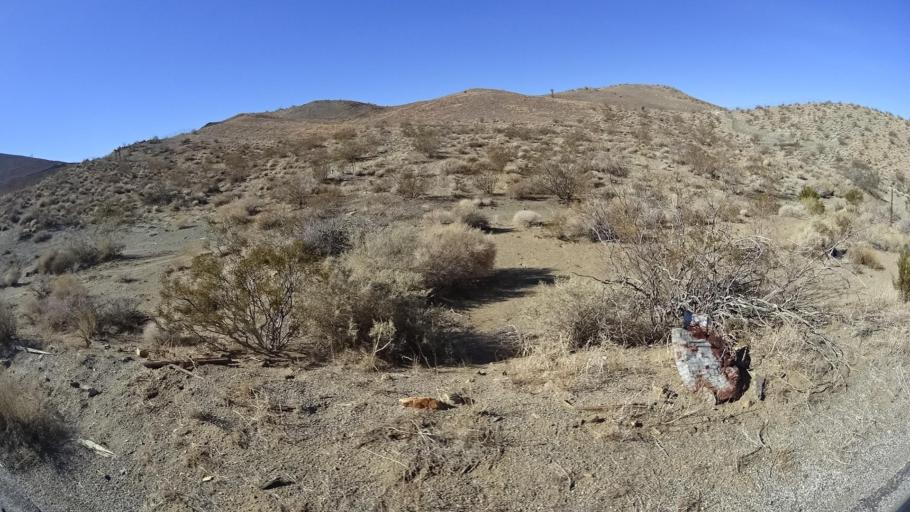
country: US
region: California
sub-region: Kern County
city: Ridgecrest
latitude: 35.3703
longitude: -117.6598
